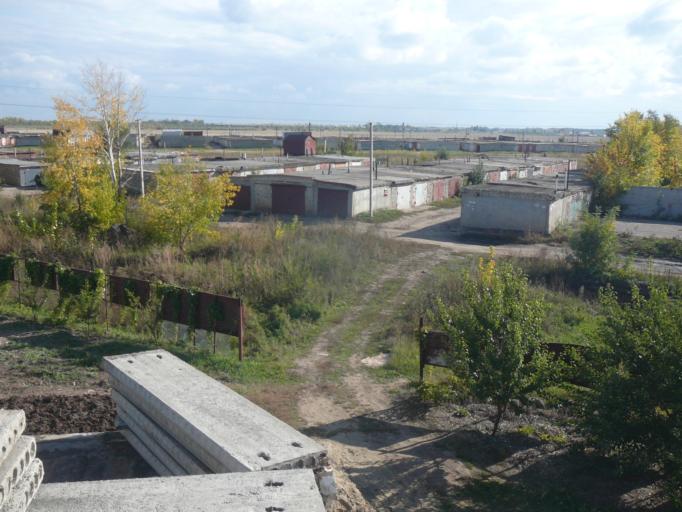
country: RU
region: Saratov
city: Engel's
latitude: 51.4958
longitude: 46.1781
